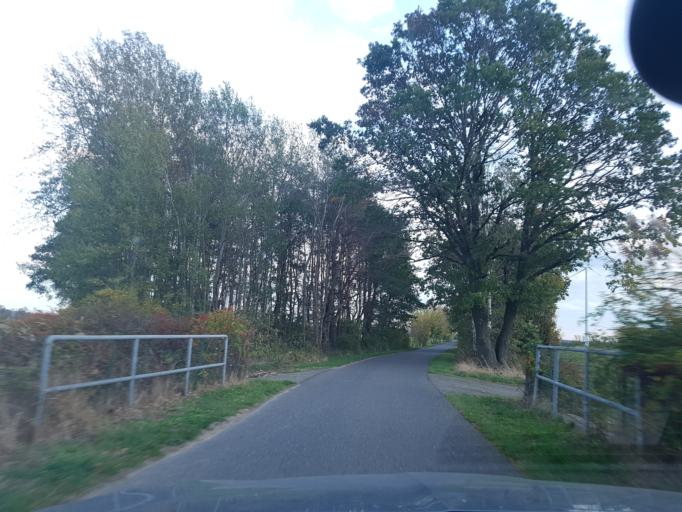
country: DE
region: Brandenburg
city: Elsterwerda
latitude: 51.4520
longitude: 13.4838
